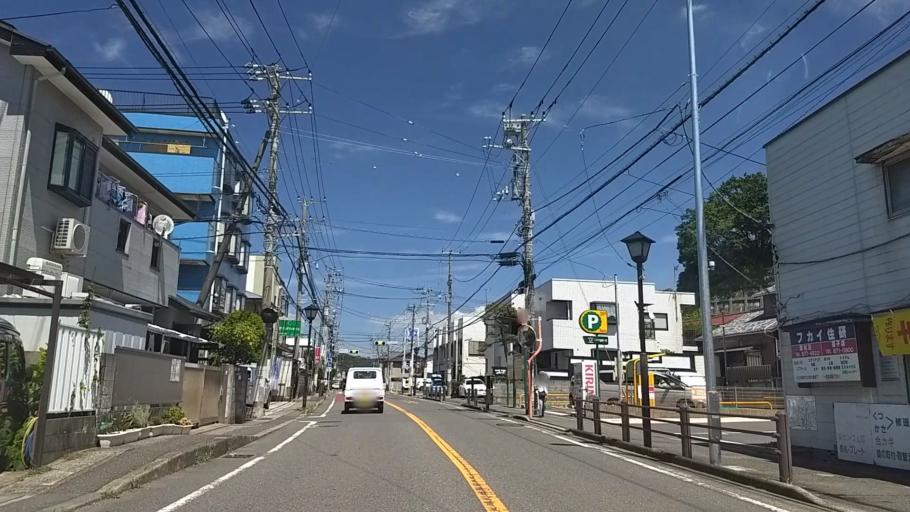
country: JP
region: Kanagawa
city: Zushi
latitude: 35.2956
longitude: 139.5894
